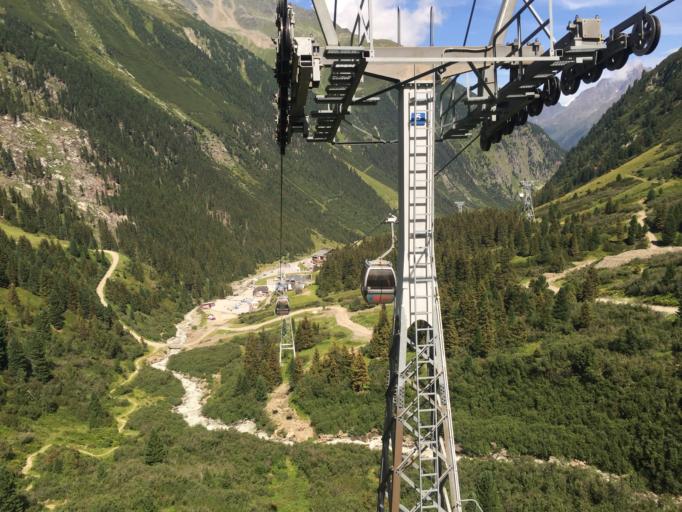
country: AT
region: Tyrol
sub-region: Politischer Bezirk Imst
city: Soelden
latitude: 47.0062
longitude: 11.1502
